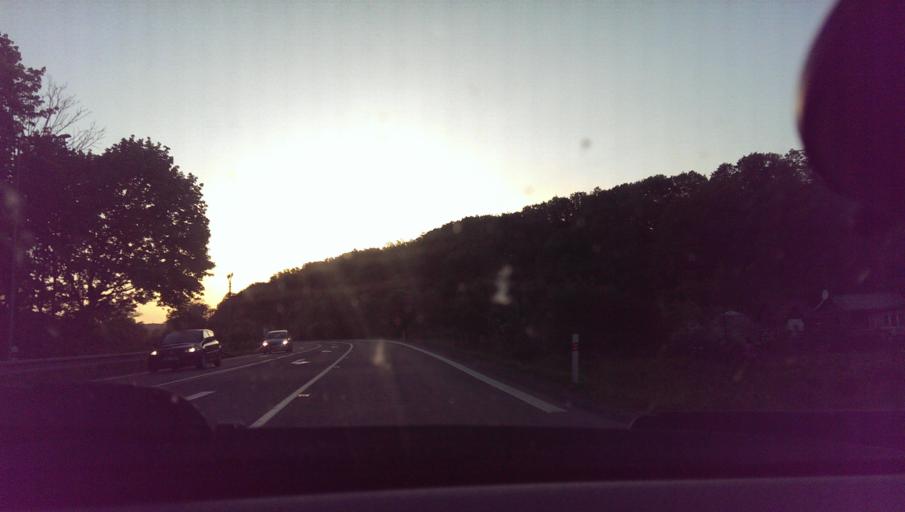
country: CZ
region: Zlin
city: Valasske Mezirici
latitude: 49.4761
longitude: 18.0037
